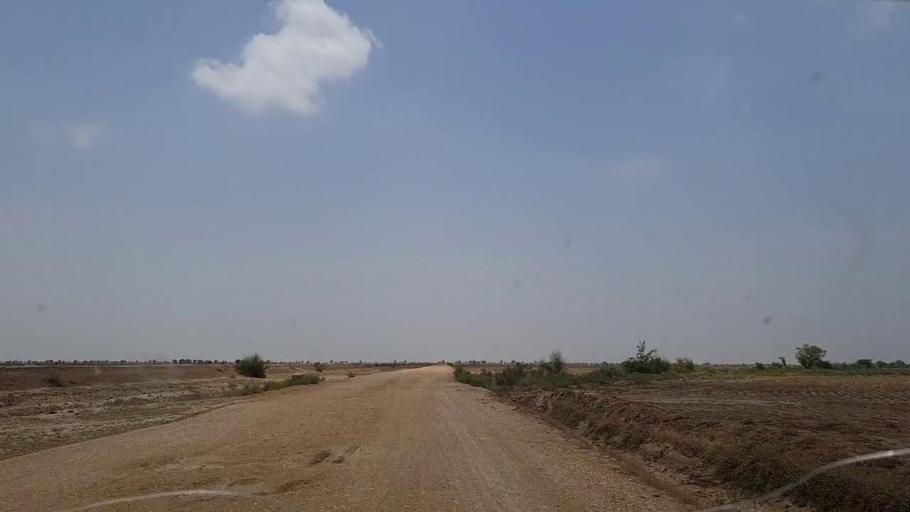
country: PK
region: Sindh
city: Phulji
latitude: 26.7913
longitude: 67.6425
